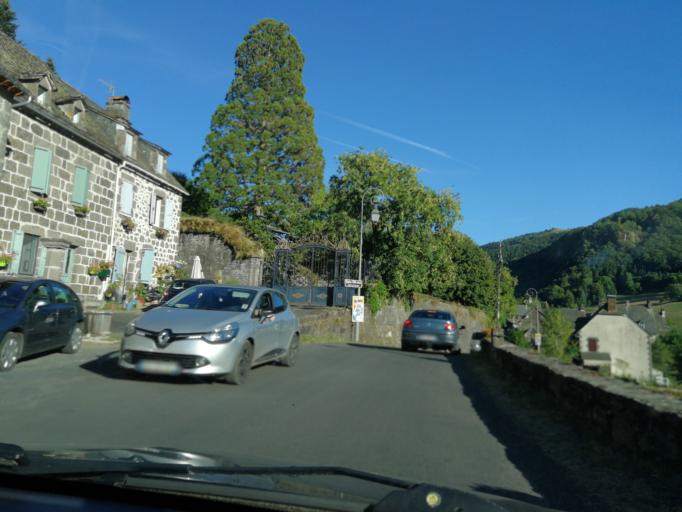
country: FR
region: Auvergne
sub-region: Departement du Cantal
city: Saint-Cernin
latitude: 45.1152
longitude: 2.5025
